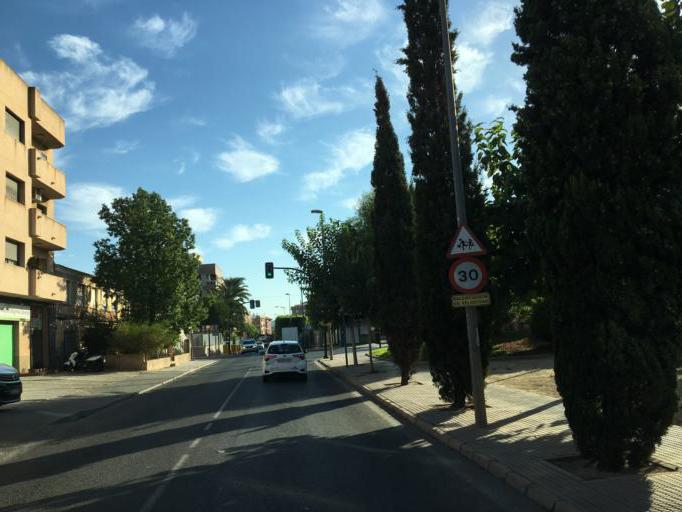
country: ES
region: Murcia
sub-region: Murcia
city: Murcia
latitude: 38.0267
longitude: -1.1275
